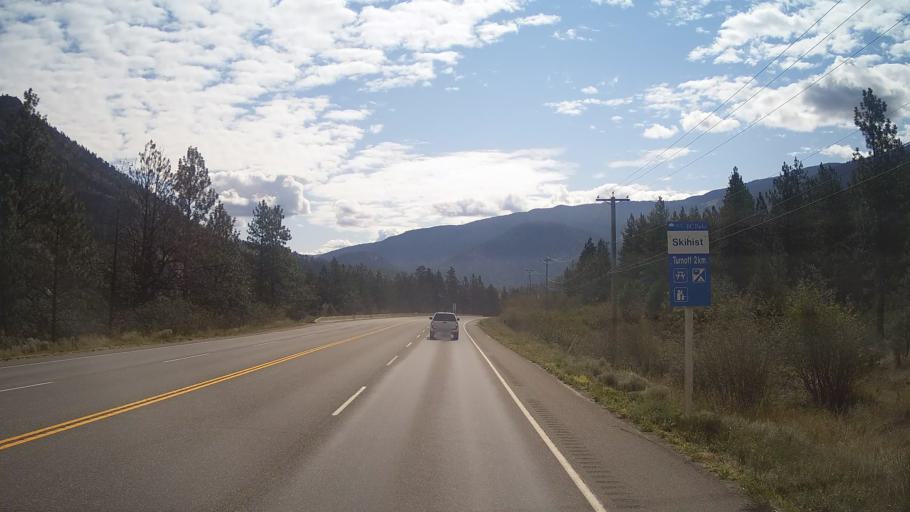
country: CA
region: British Columbia
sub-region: Thompson-Nicola Regional District
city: Ashcroft
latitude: 50.2587
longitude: -121.5309
